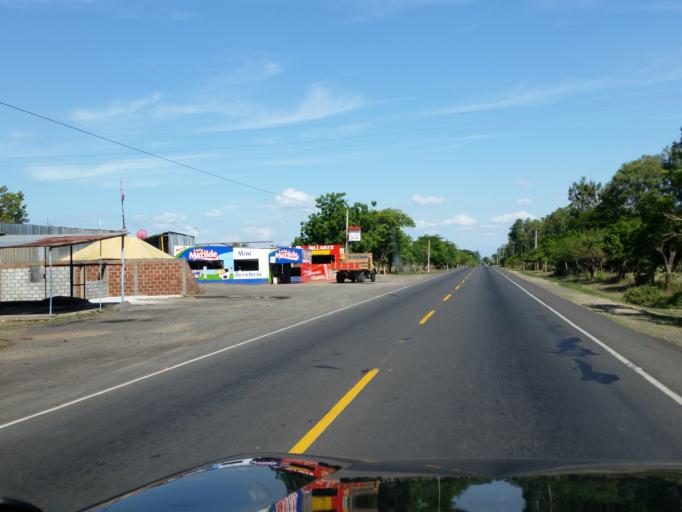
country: NI
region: Leon
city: La Paz Centro
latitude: 12.3299
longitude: -86.8049
